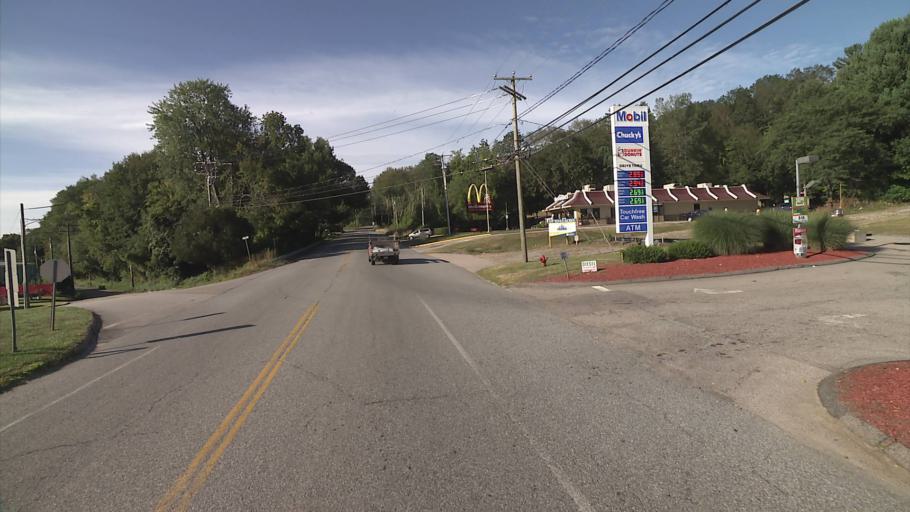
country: US
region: Connecticut
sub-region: New London County
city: Uncasville
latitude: 41.4413
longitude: -72.1059
